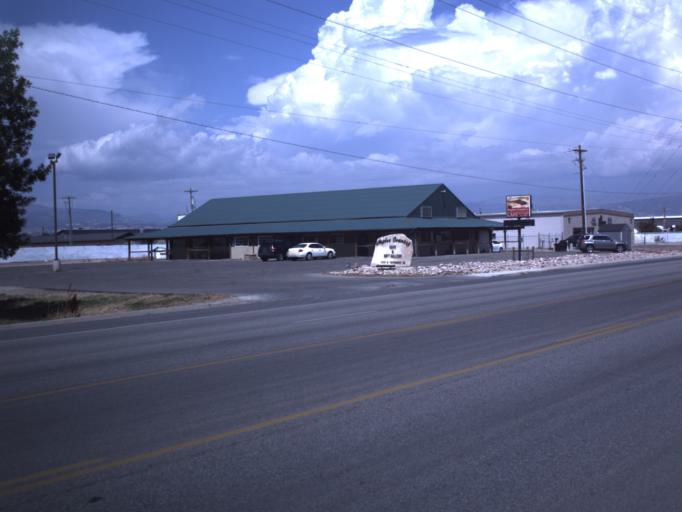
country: US
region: Utah
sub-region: Uintah County
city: Naples
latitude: 40.4405
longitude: -109.4996
